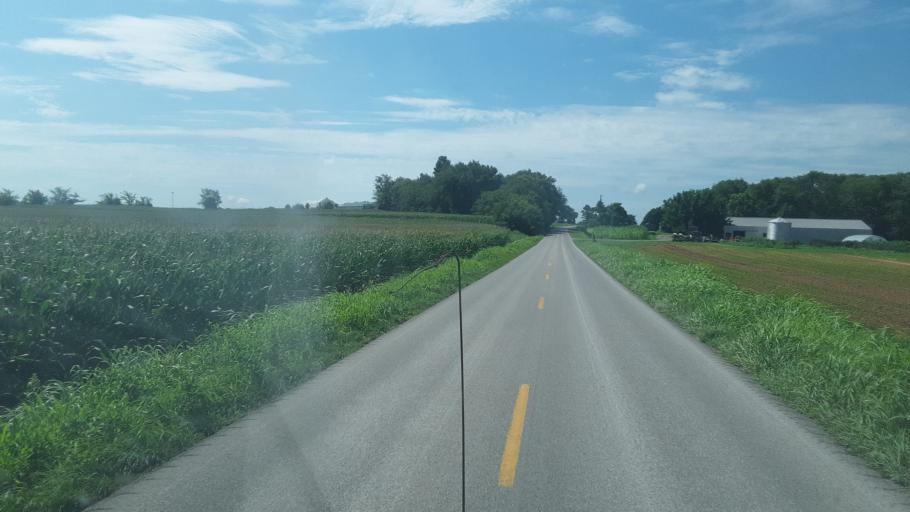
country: US
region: Kentucky
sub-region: Todd County
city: Elkton
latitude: 36.8157
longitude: -87.3143
